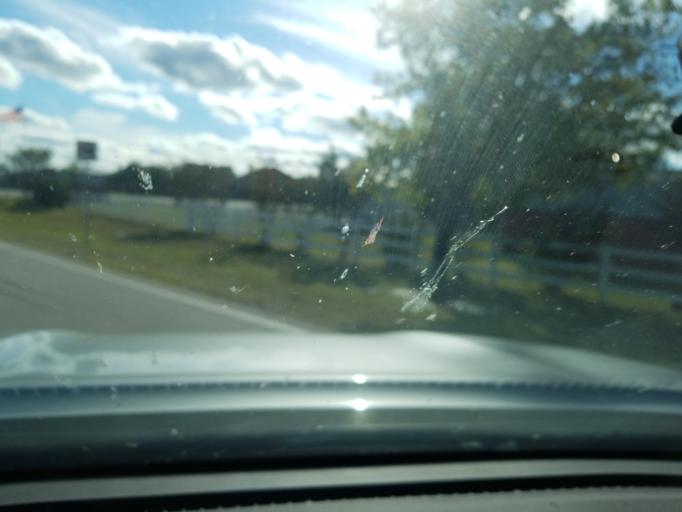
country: US
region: Texas
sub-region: Tarrant County
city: Pecan Acres
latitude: 32.9920
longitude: -97.4154
